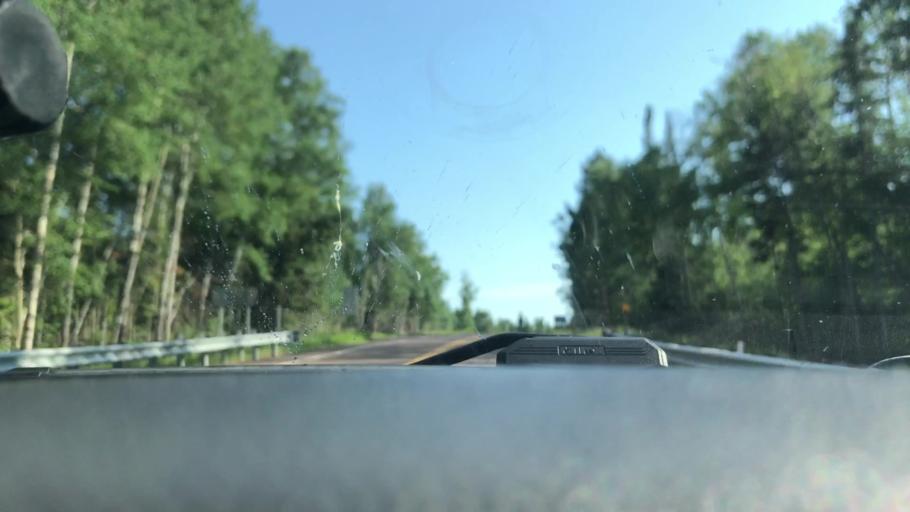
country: US
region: Minnesota
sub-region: Cook County
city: Grand Marais
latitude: 47.8362
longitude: -89.9734
